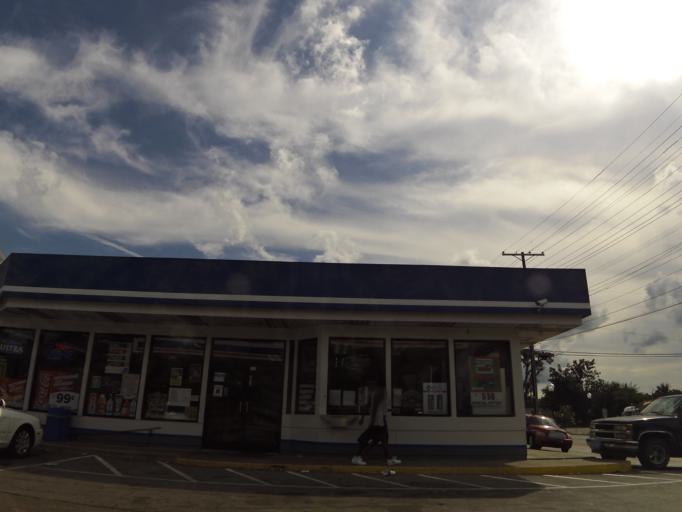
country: US
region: Kentucky
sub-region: Christian County
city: Hopkinsville
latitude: 36.8631
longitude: -87.4841
